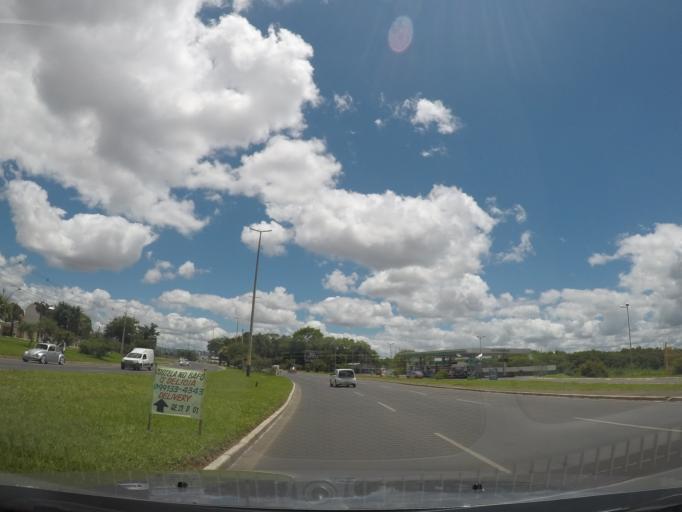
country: BR
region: Federal District
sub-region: Brasilia
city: Brasilia
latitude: -15.8454
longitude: -47.9670
